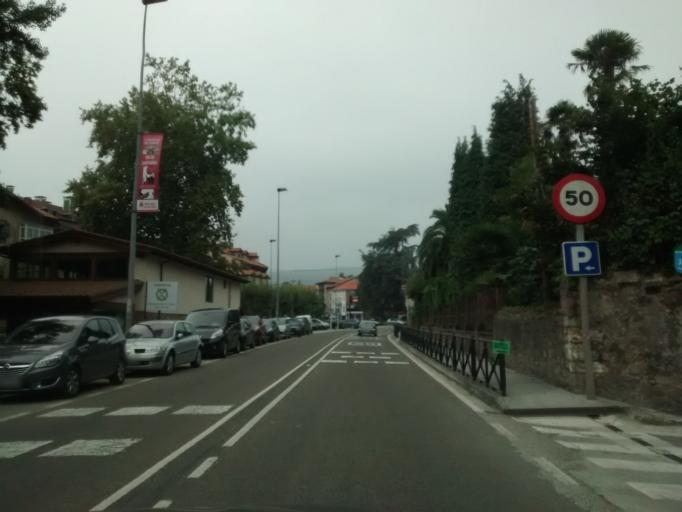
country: ES
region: Cantabria
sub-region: Provincia de Cantabria
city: Cabezon de la Sal
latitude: 43.3099
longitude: -4.2336
